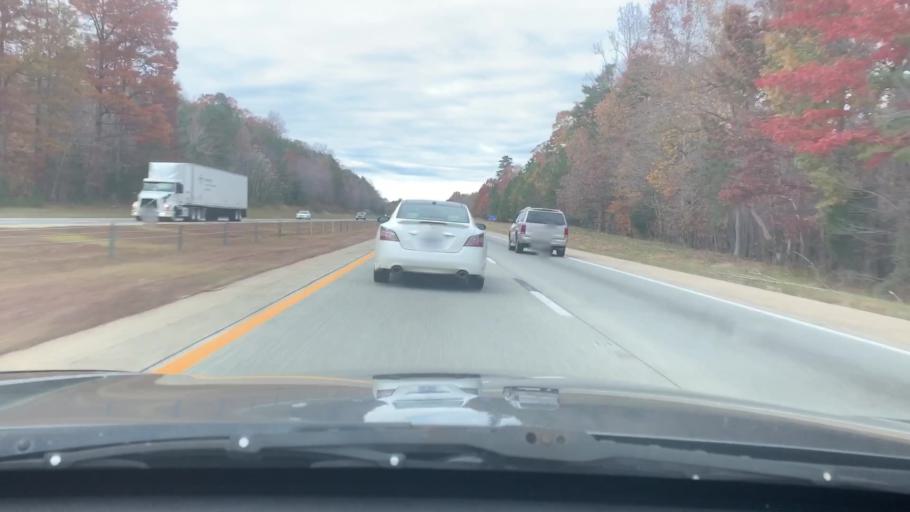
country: US
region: North Carolina
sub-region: Orange County
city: Hillsborough
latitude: 36.0243
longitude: -79.0886
